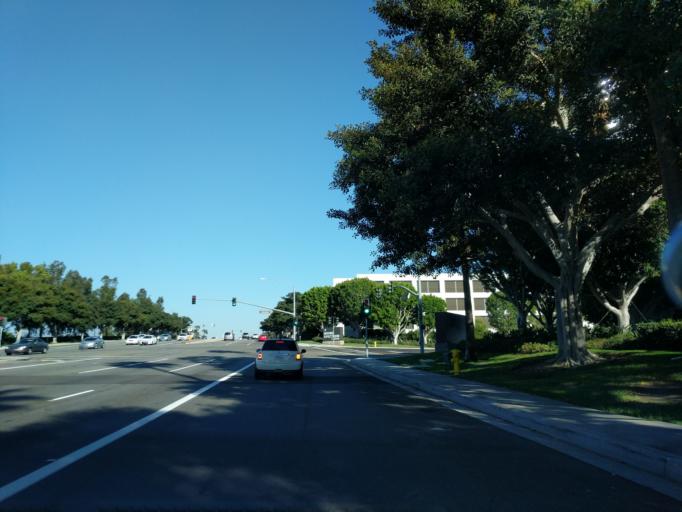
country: US
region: California
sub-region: Orange County
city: Laguna Woods
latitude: 33.6552
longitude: -117.7475
